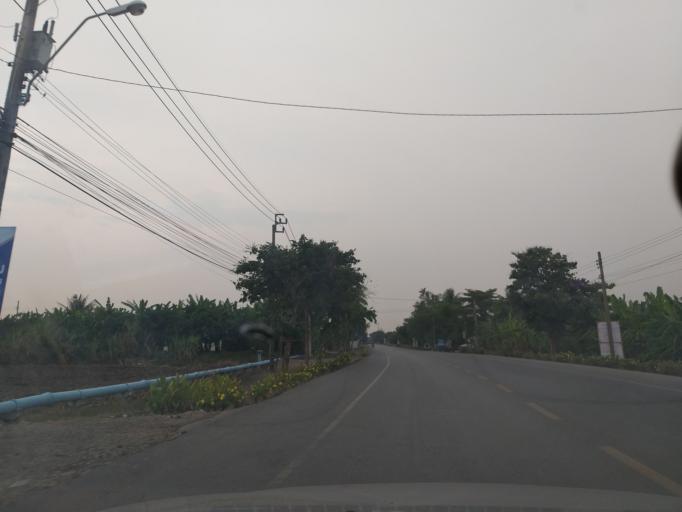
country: TH
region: Bangkok
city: Nong Chok
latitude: 13.8180
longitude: 100.9316
